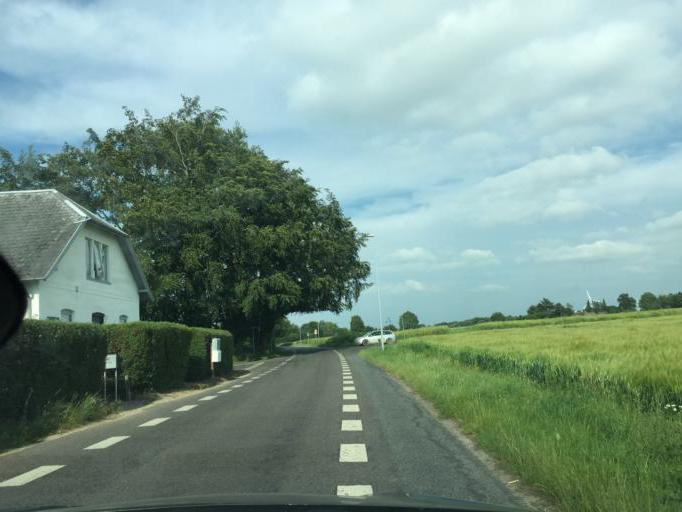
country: DK
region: South Denmark
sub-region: Faaborg-Midtfyn Kommune
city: Arslev
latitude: 55.3135
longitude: 10.5277
